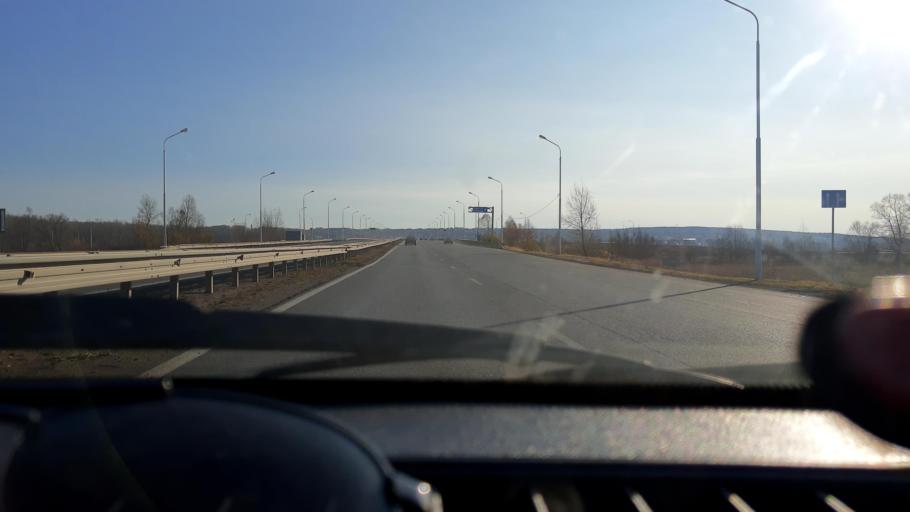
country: RU
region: Bashkortostan
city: Kabakovo
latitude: 54.6552
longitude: 56.0820
